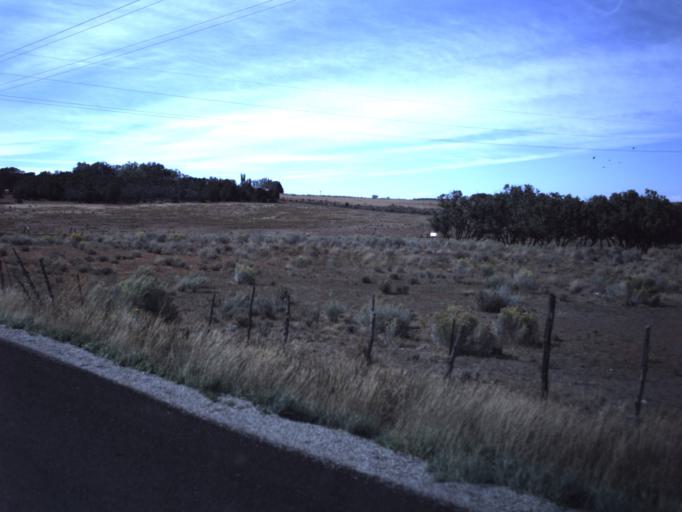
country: US
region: Utah
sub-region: San Juan County
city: Monticello
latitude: 37.8728
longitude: -109.3181
